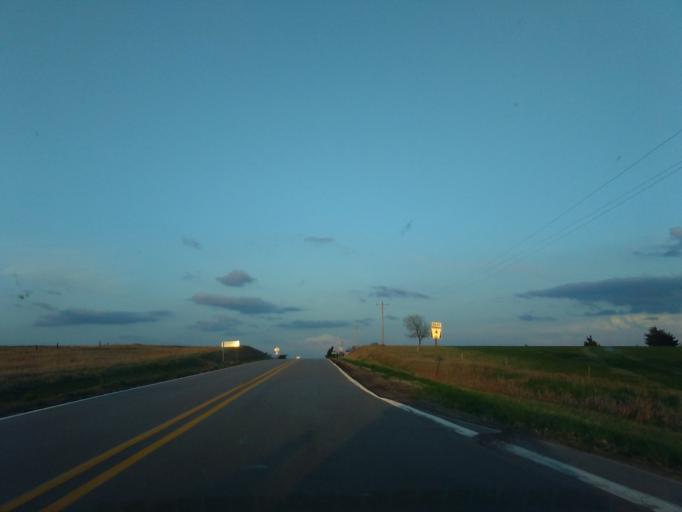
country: US
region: Nebraska
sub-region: Nuckolls County
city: Nelson
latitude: 40.2924
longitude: -98.3301
